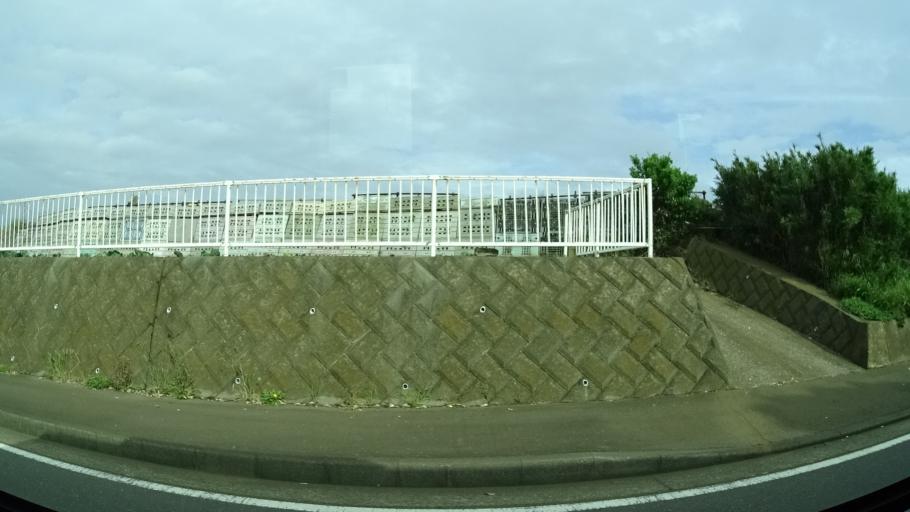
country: JP
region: Kanagawa
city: Miura
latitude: 35.1541
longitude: 139.6691
